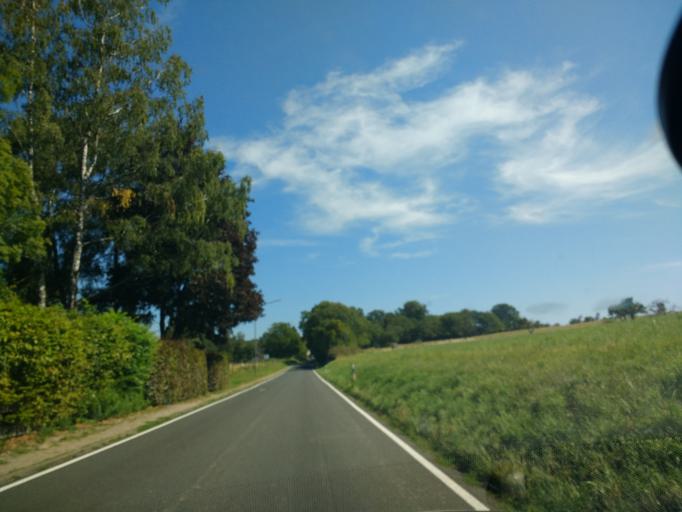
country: DE
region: Rheinland-Pfalz
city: Fisch
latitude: 49.6223
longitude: 6.4587
